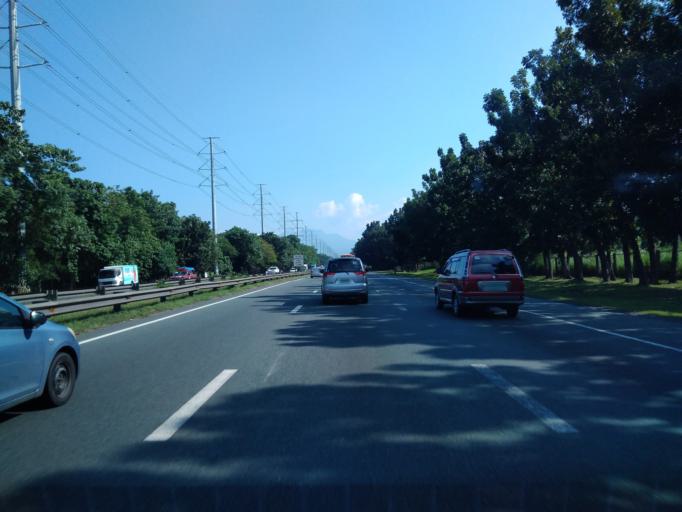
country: PH
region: Calabarzon
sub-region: Province of Laguna
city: Cabuyao
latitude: 14.2475
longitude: 121.1078
